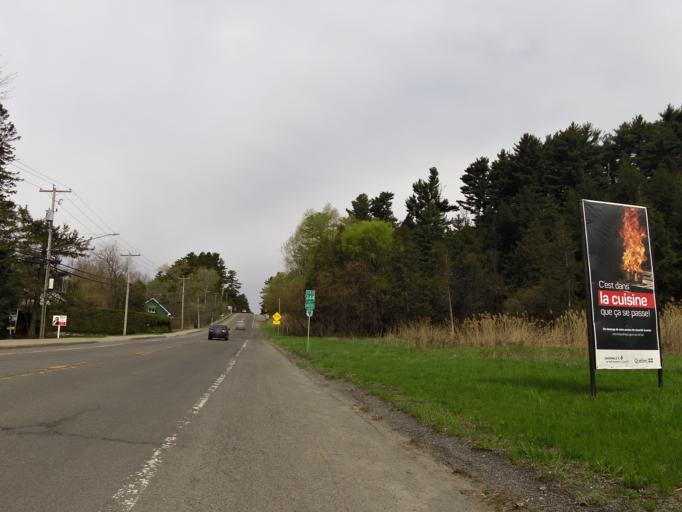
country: CA
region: Quebec
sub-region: Laurentides
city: Oka
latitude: 45.4627
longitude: -74.0963
